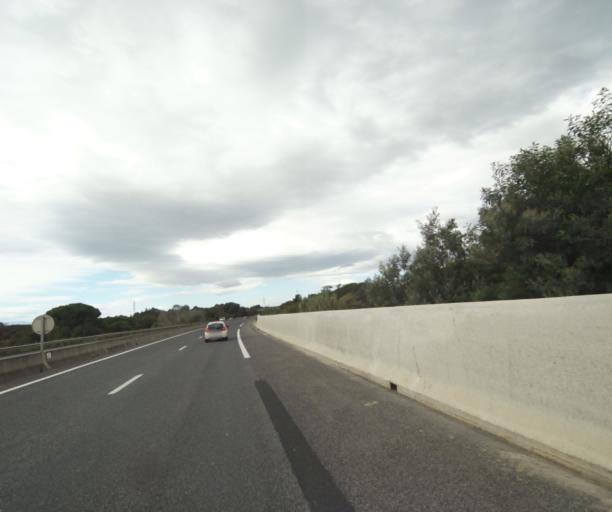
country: FR
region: Languedoc-Roussillon
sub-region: Departement des Pyrenees-Orientales
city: Argelers
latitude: 42.5426
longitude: 3.0131
